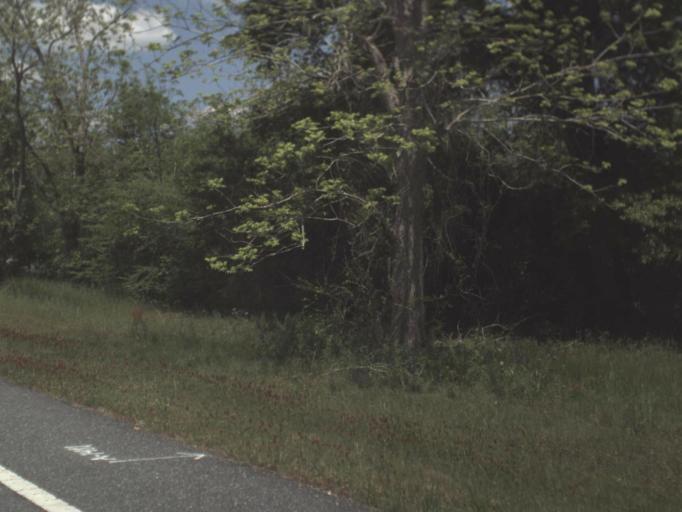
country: US
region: Florida
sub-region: Santa Rosa County
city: Point Baker
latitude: 30.8383
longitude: -87.0499
